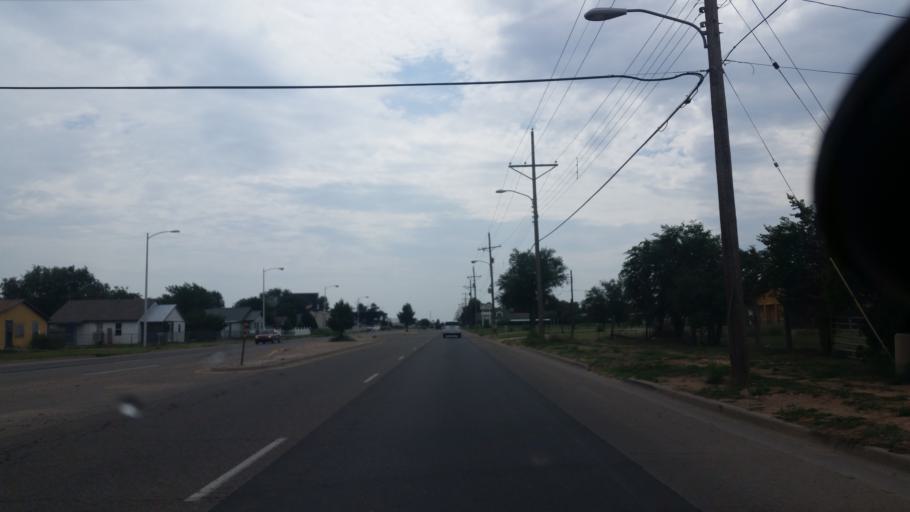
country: US
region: New Mexico
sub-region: Curry County
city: Clovis
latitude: 34.3847
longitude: -103.1966
